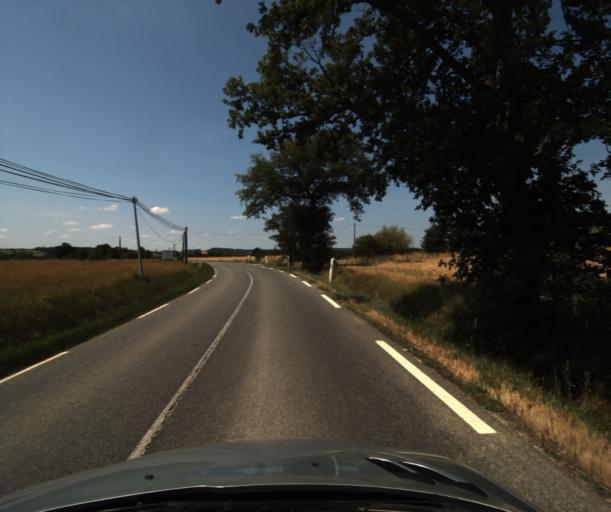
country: FR
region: Midi-Pyrenees
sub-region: Departement de la Haute-Garonne
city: Saint-Lys
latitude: 43.5294
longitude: 1.1718
